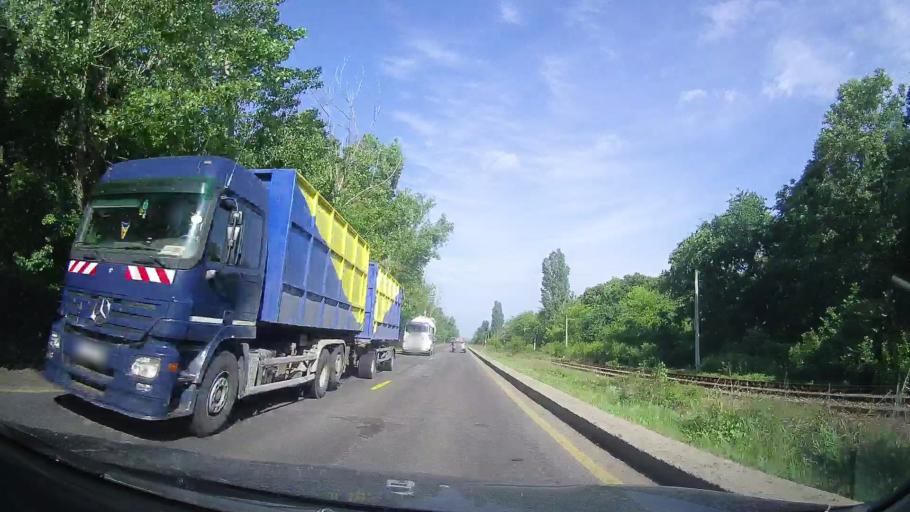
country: RO
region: Ilfov
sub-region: Comuna Magurele
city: Alunisu
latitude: 44.3546
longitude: 26.0506
